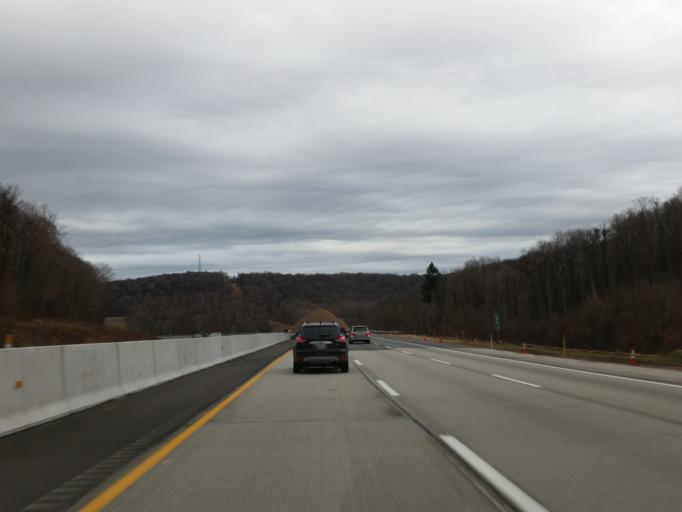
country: US
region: Pennsylvania
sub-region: Westmoreland County
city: Ligonier
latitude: 40.1063
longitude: -79.2403
